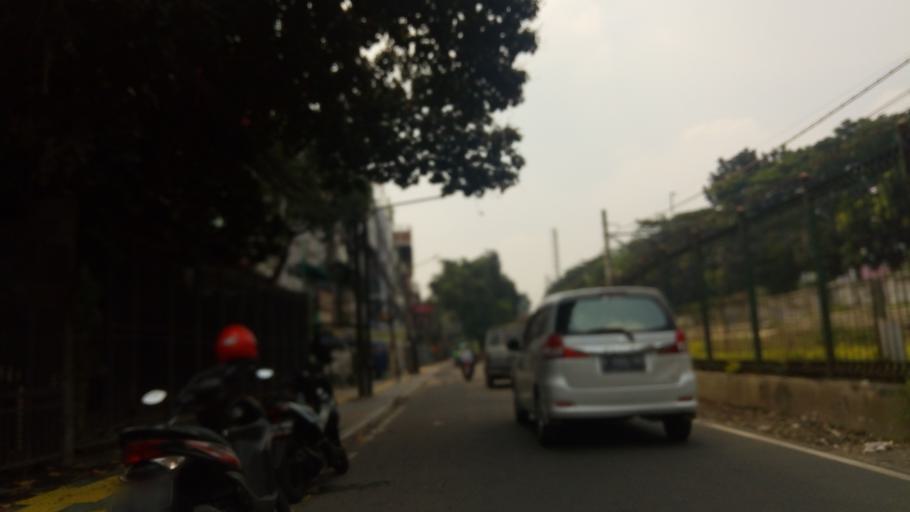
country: ID
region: Jakarta Raya
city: Jakarta
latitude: -6.2029
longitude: 106.8260
